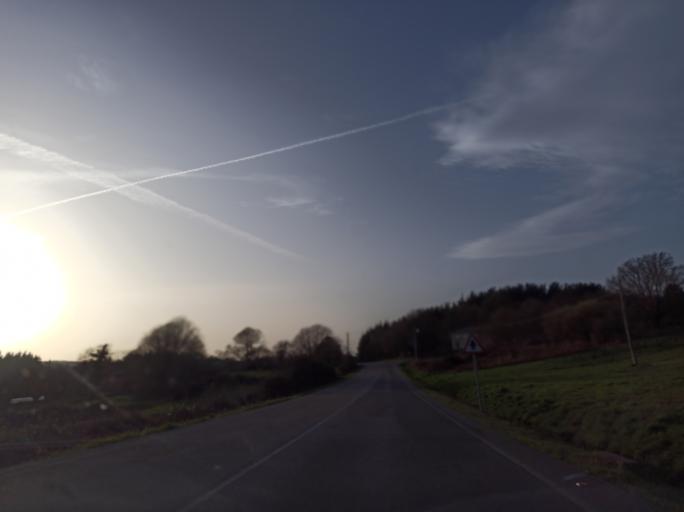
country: ES
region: Galicia
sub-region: Provincia de Lugo
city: Friol
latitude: 43.0212
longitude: -7.8222
